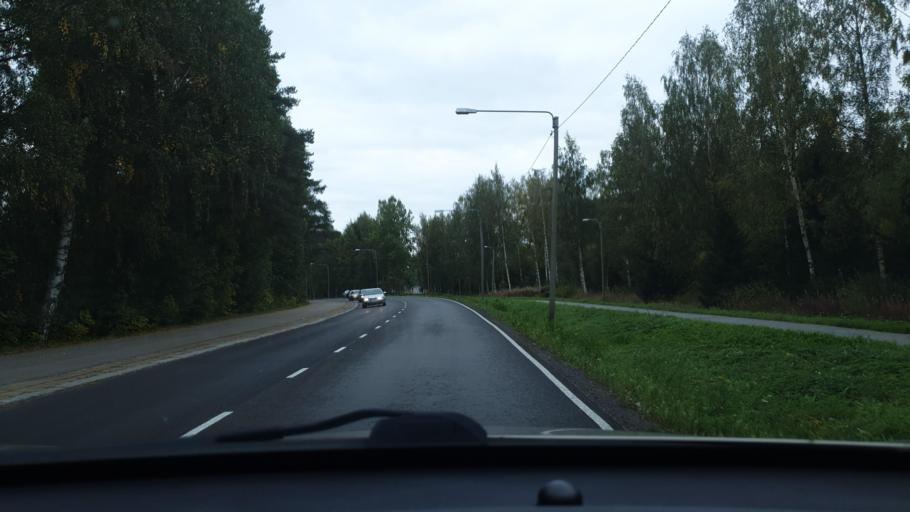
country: FI
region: Ostrobothnia
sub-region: Vaasa
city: Teeriniemi
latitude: 63.0886
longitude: 21.6911
